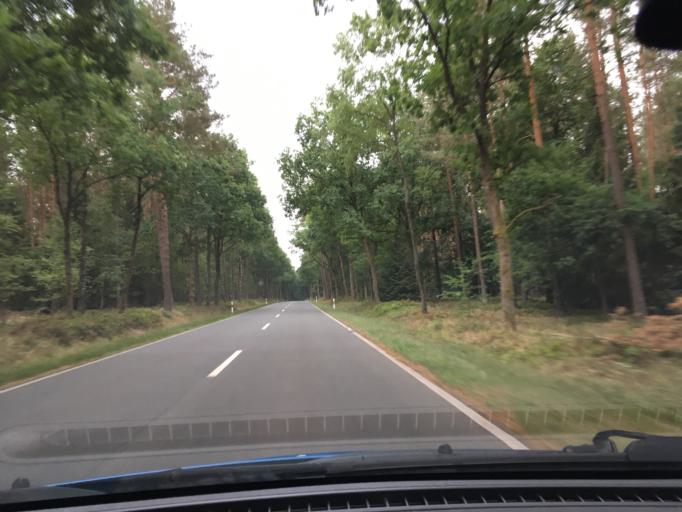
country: DE
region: Lower Saxony
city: Scharnhorst
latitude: 52.7736
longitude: 10.3037
